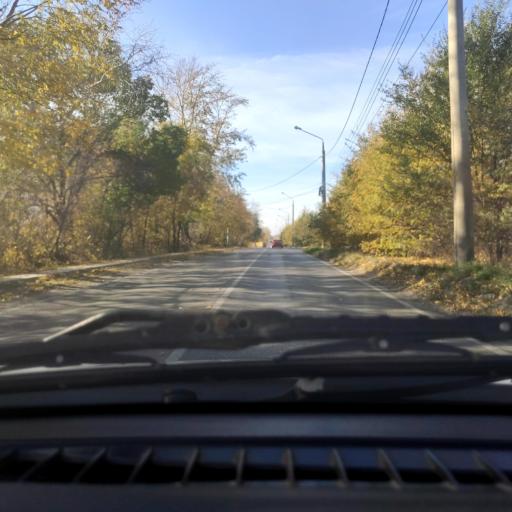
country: RU
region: Samara
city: Zhigulevsk
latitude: 53.4635
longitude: 49.5610
